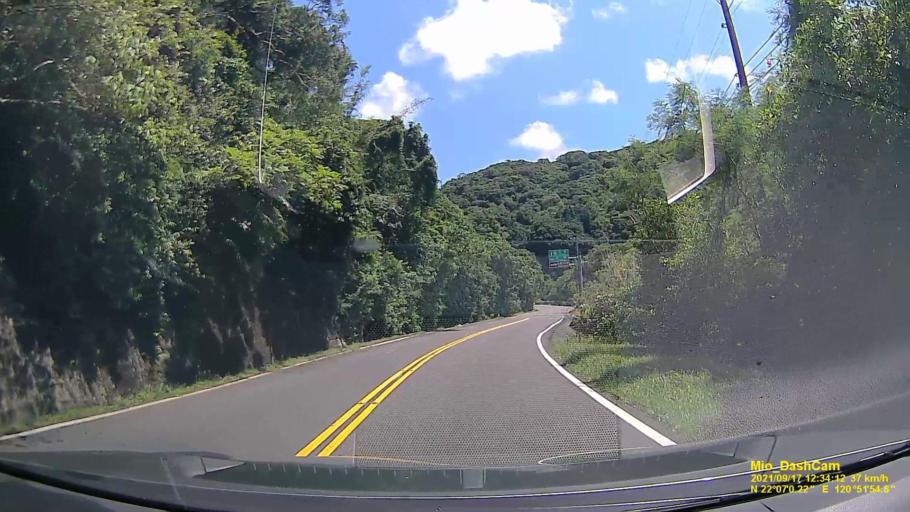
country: TW
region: Taiwan
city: Hengchun
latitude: 22.1167
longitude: 120.8652
